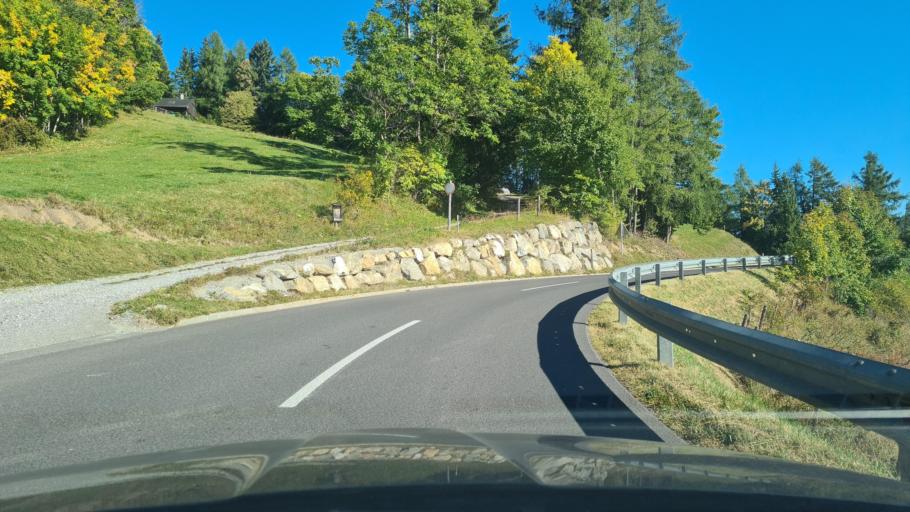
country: AT
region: Styria
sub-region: Politischer Bezirk Weiz
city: Passail
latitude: 47.3294
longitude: 15.4748
